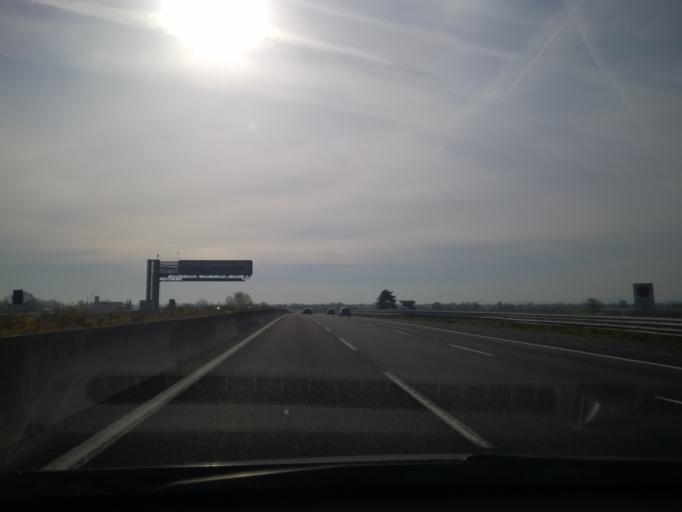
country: IT
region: Emilia-Romagna
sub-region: Provincia di Ravenna
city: Granarolo
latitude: 44.3202
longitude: 11.9140
